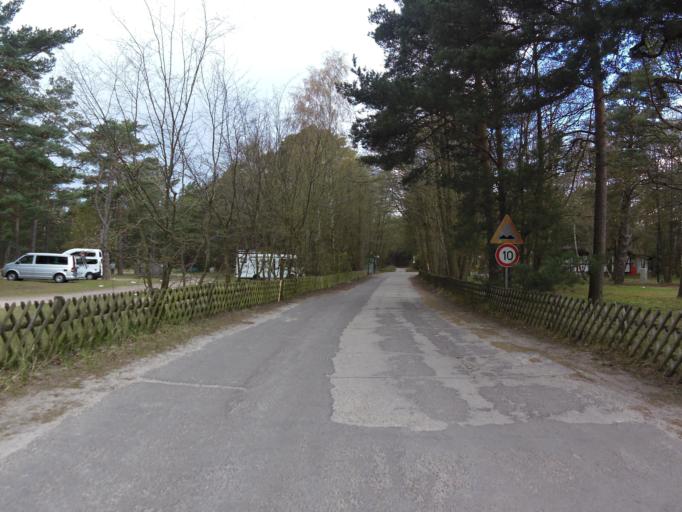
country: DE
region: Mecklenburg-Vorpommern
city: Ostseebad Prerow
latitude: 54.4573
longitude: 12.5379
